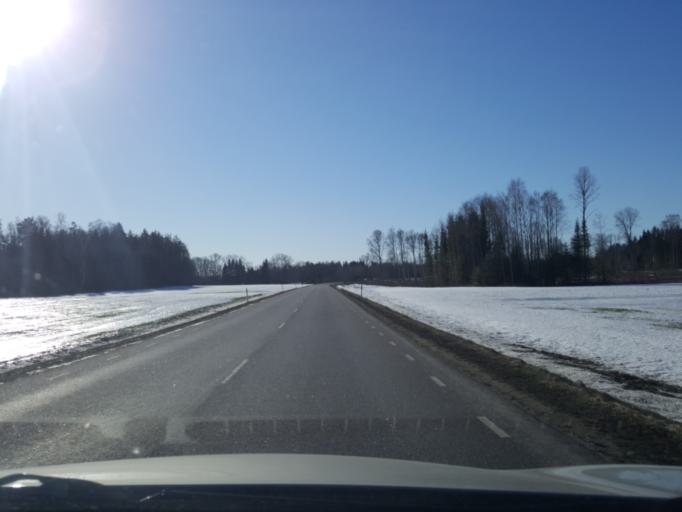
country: EE
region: Viljandimaa
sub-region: Viiratsi vald
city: Viiratsi
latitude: 58.4254
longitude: 25.6828
